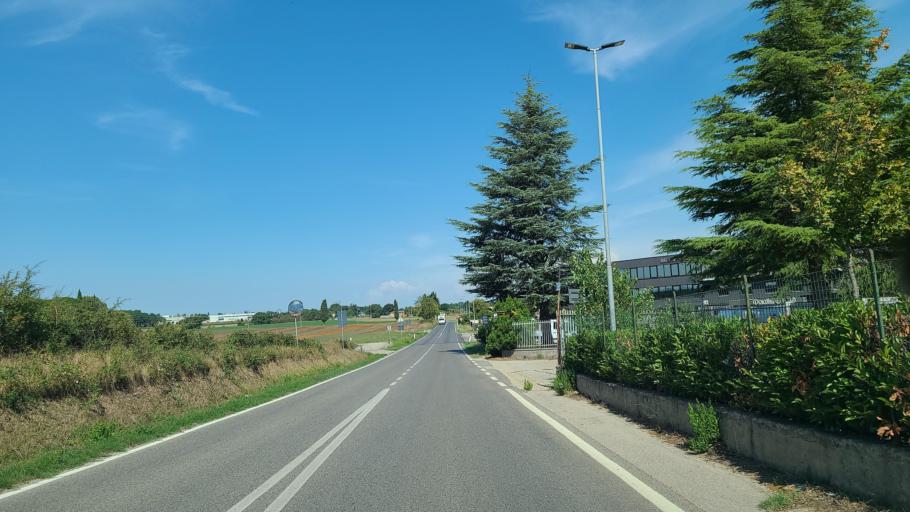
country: IT
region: Tuscany
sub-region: Provincia di Siena
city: Staggia
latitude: 43.3987
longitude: 11.1770
